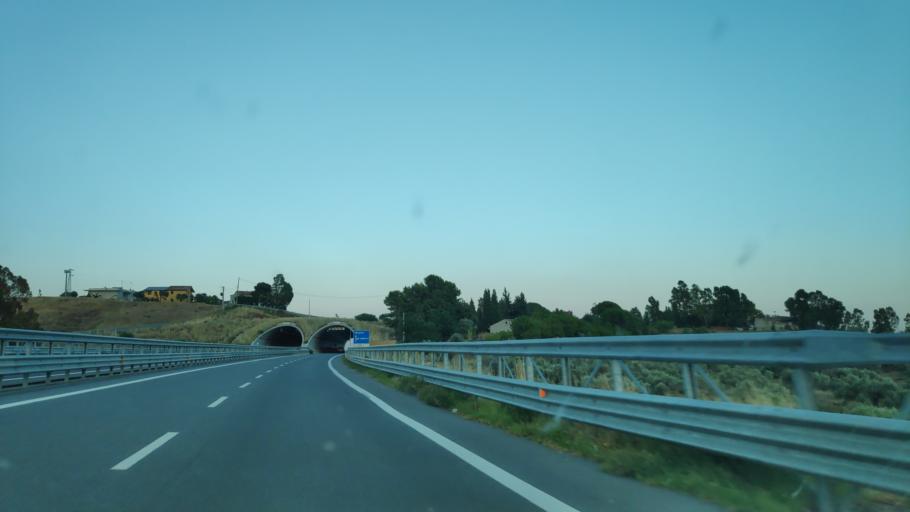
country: IT
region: Calabria
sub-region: Provincia di Reggio Calabria
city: Marina di Gioiosa Ionica
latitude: 38.3121
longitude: 16.3413
